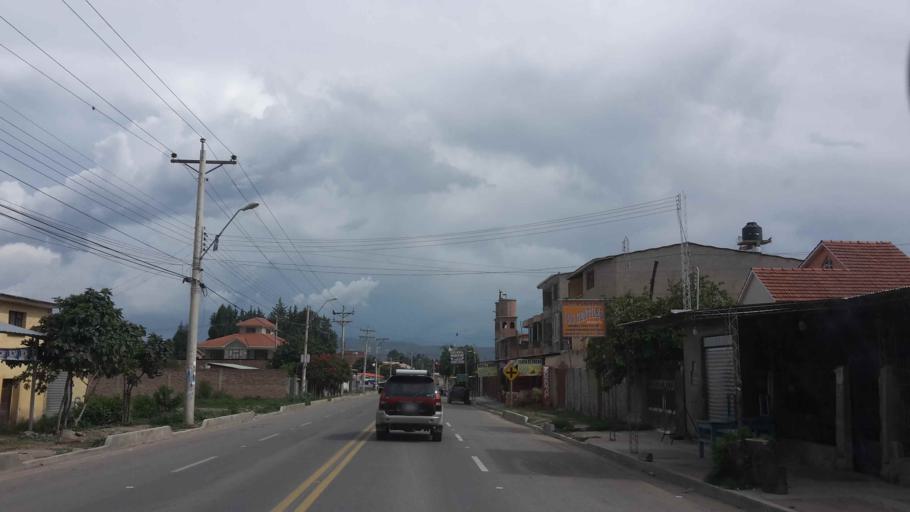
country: BO
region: Cochabamba
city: Cochabamba
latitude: -17.3591
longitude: -66.2534
